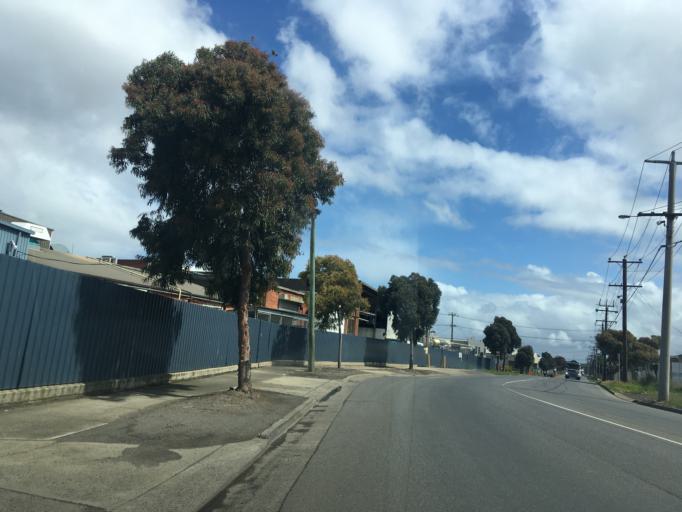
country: AU
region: Victoria
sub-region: Brimbank
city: Brooklyn
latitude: -37.8207
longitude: 144.8160
